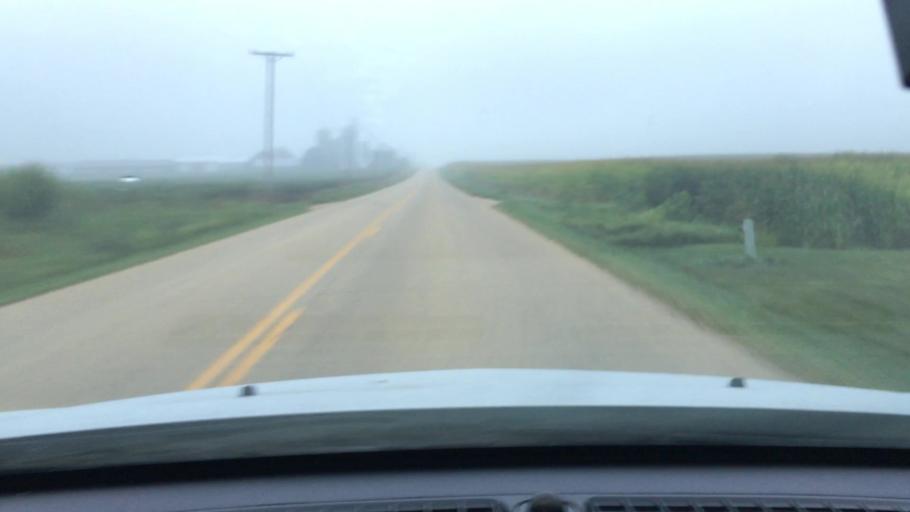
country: US
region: Illinois
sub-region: DeKalb County
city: Malta
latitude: 41.8554
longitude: -88.9613
